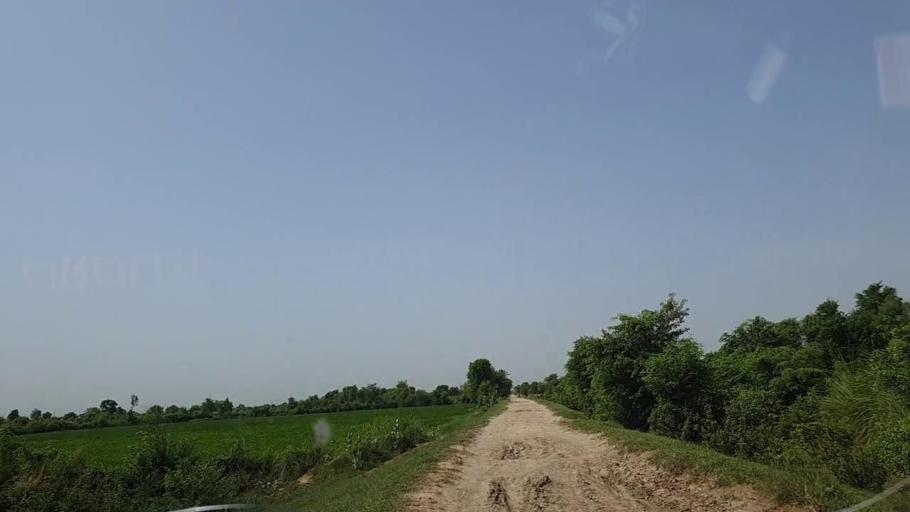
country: PK
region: Sindh
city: Naushahro Firoz
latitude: 26.8630
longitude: 68.0308
